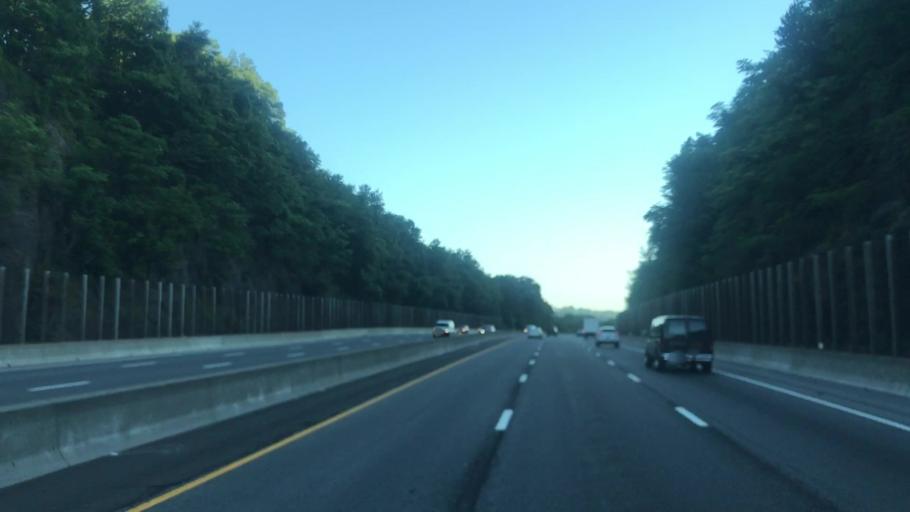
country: US
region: New York
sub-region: Westchester County
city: Ardsley
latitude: 40.9949
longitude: -73.8539
